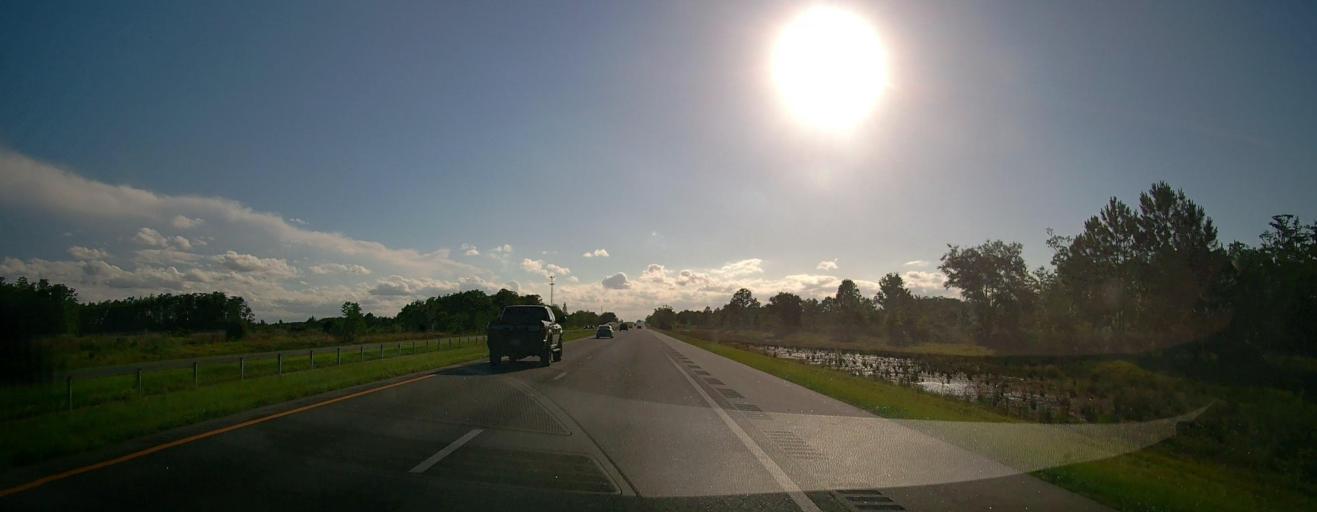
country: US
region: Florida
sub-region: Orange County
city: Wedgefield
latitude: 28.4517
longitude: -81.1325
